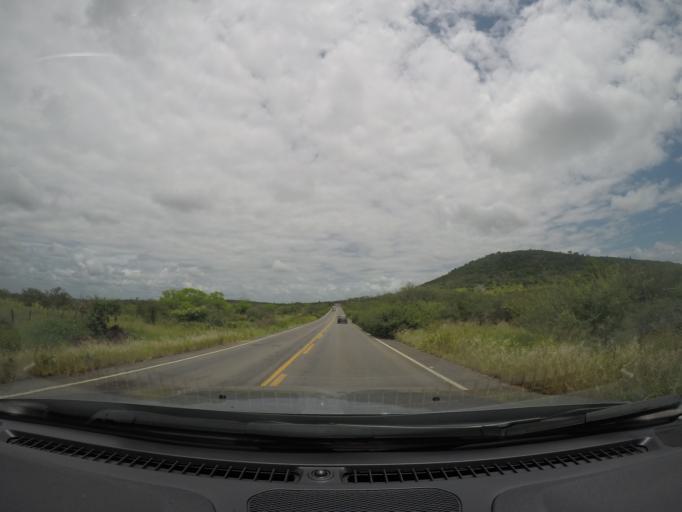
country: BR
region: Bahia
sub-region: Itaberaba
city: Itaberaba
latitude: -12.5026
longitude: -40.2492
